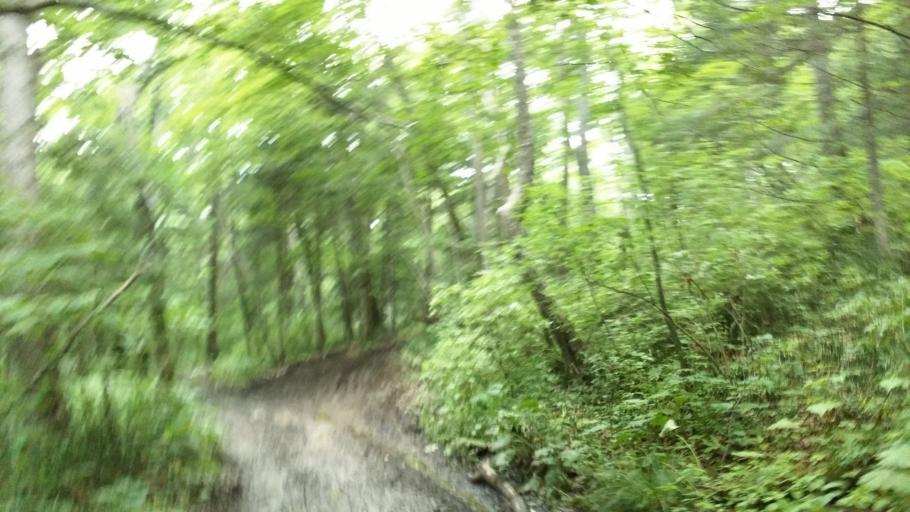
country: RU
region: Primorskiy
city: Trudovoye
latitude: 43.2062
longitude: 132.0090
